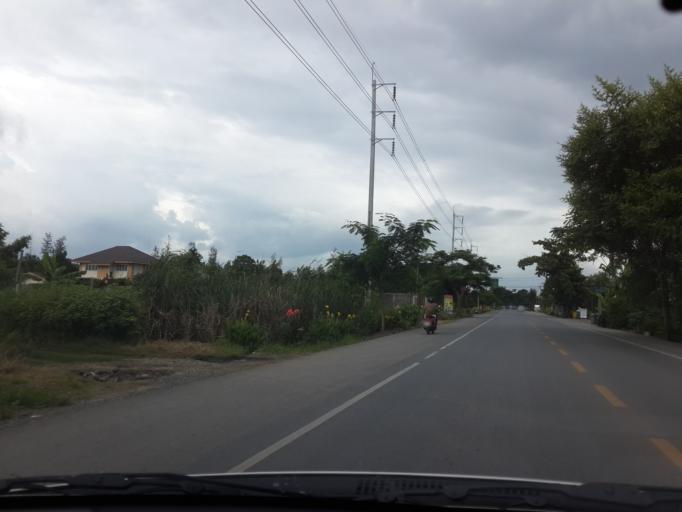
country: TH
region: Bangkok
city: Khlong Sam Wa
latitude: 13.8337
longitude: 100.7650
